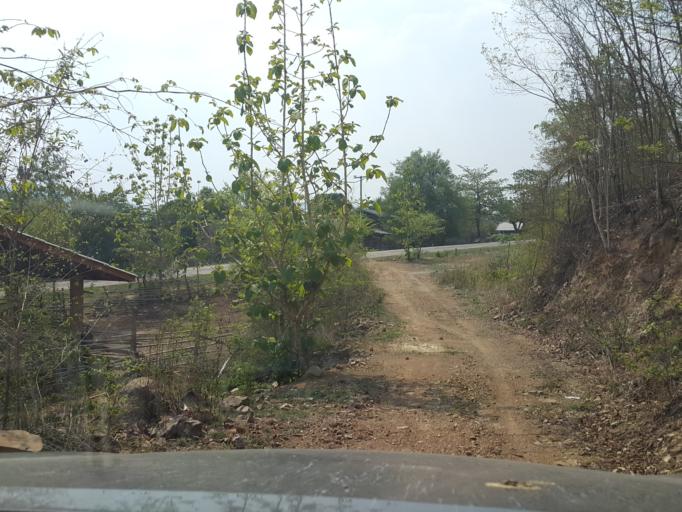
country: TH
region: Lampang
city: Mae Phrik
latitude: 17.5284
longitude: 98.9958
